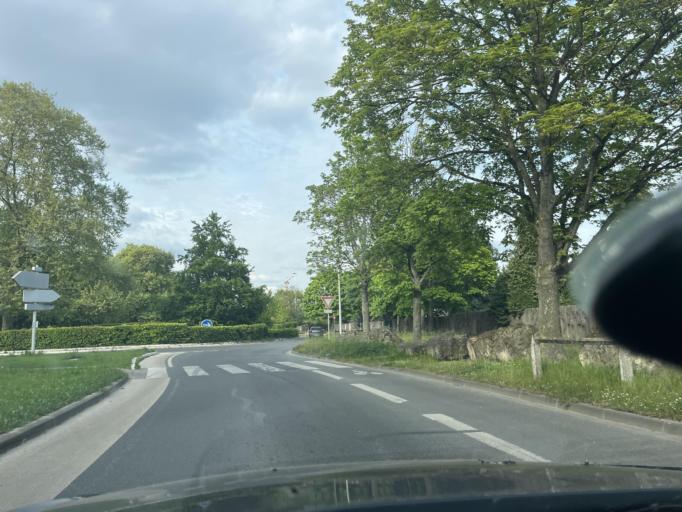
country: FR
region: Ile-de-France
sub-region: Departement de Seine-Saint-Denis
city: La Courneuve
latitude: 48.9394
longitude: 2.4071
